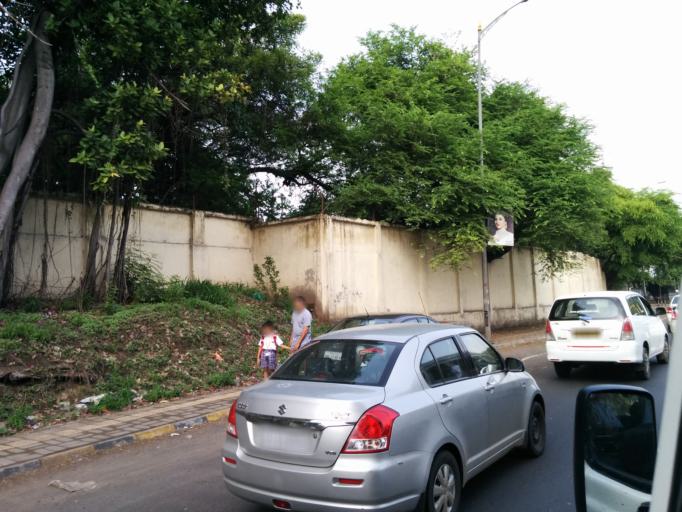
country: IN
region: Maharashtra
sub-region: Pune Division
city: Pune
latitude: 18.5066
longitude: 73.8976
